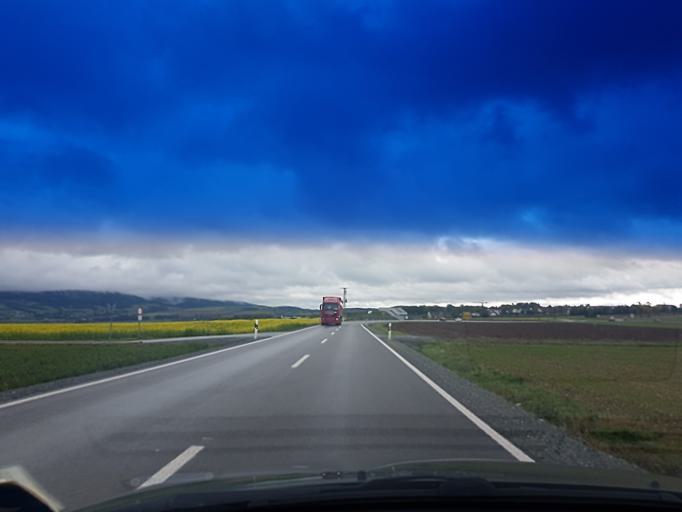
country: DE
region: Bavaria
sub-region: Upper Franconia
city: Bindlach
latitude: 50.0056
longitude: 11.6213
